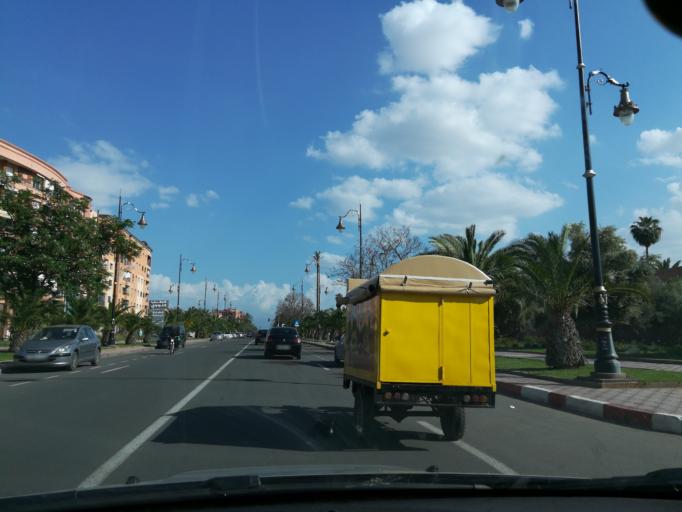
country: MA
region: Marrakech-Tensift-Al Haouz
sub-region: Marrakech
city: Marrakesh
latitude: 31.6359
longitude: -8.0199
